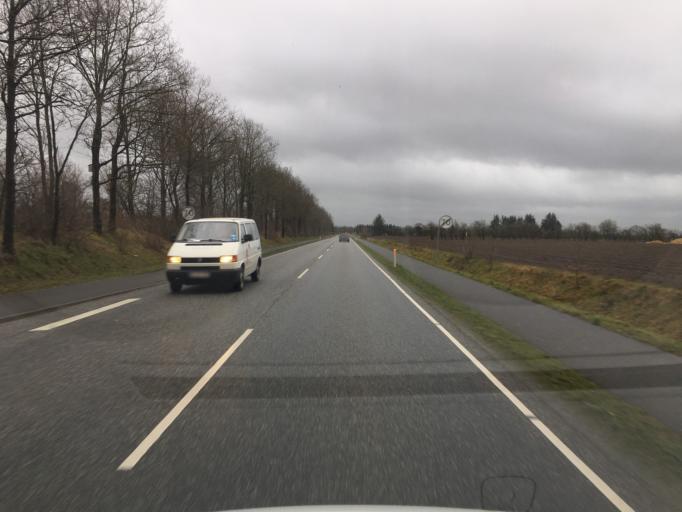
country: DK
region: South Denmark
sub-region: Aabenraa Kommune
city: Tinglev
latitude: 54.9272
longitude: 9.2426
